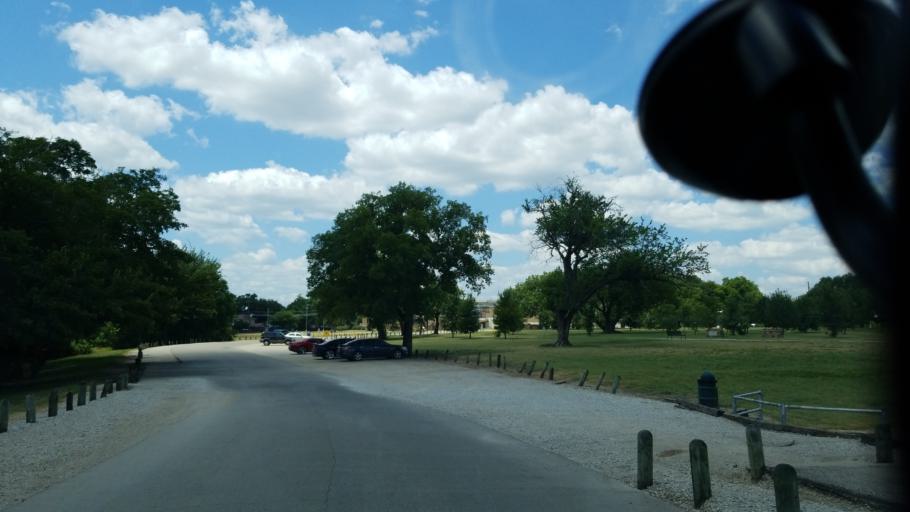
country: US
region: Texas
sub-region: Dallas County
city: Cockrell Hill
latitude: 32.7133
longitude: -96.8548
